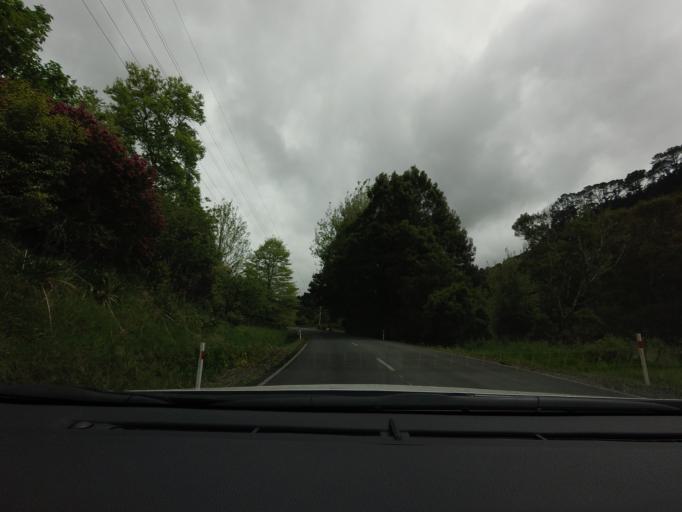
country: NZ
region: Auckland
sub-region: Auckland
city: Warkworth
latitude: -36.4946
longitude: 174.6260
